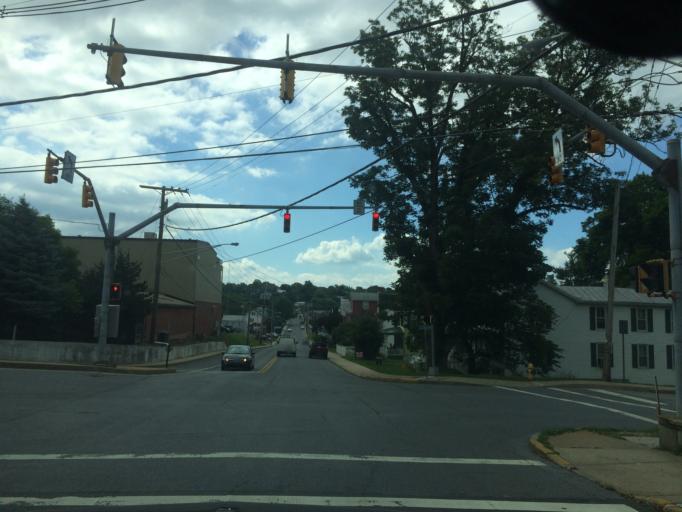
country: US
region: Maryland
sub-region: Carroll County
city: Westminster
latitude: 39.5702
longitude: -76.9931
